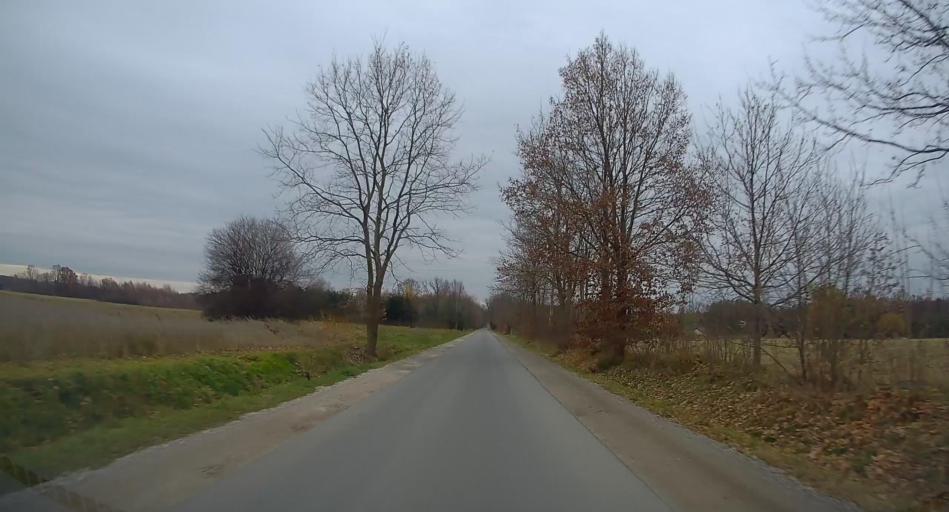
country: PL
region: Lodz Voivodeship
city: Zabia Wola
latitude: 52.0040
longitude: 20.6571
